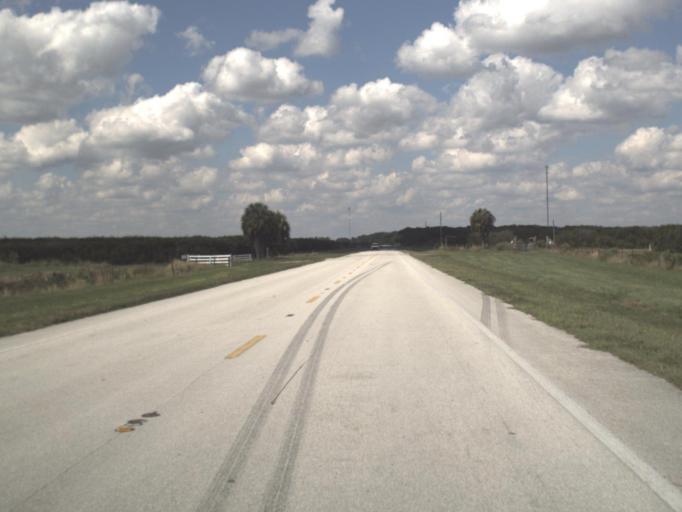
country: US
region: Florida
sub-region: Highlands County
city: Sebring
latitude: 27.4185
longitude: -81.5691
